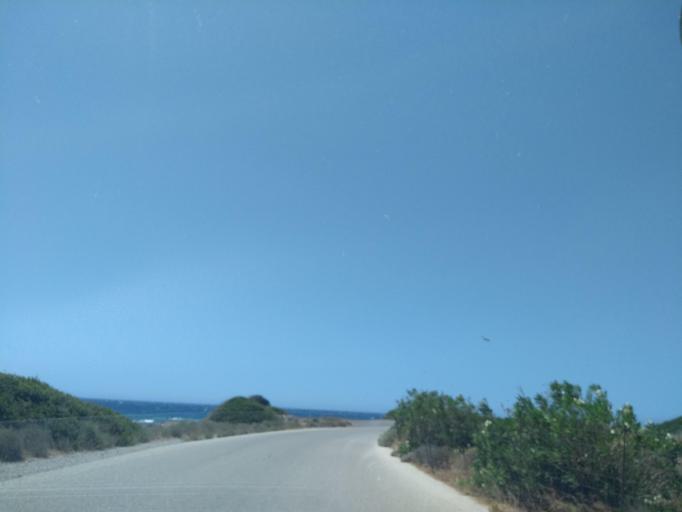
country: GR
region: Crete
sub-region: Nomos Chanias
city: Vryses
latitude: 35.3538
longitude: 23.5343
